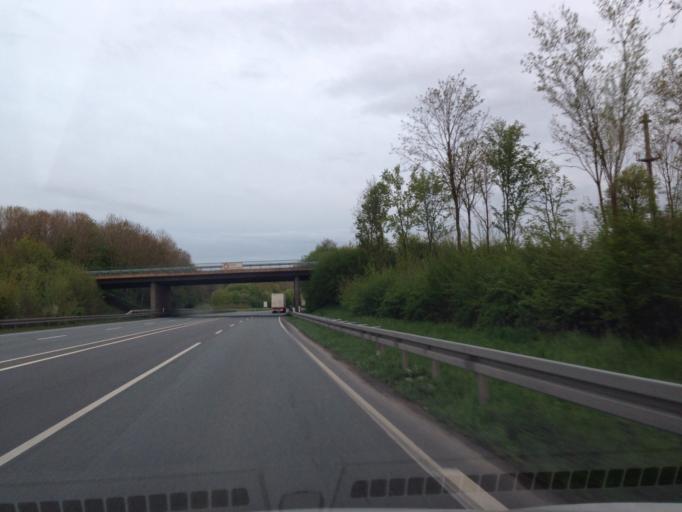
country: DE
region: North Rhine-Westphalia
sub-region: Regierungsbezirk Munster
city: Altenberge
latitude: 52.0717
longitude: 7.4317
